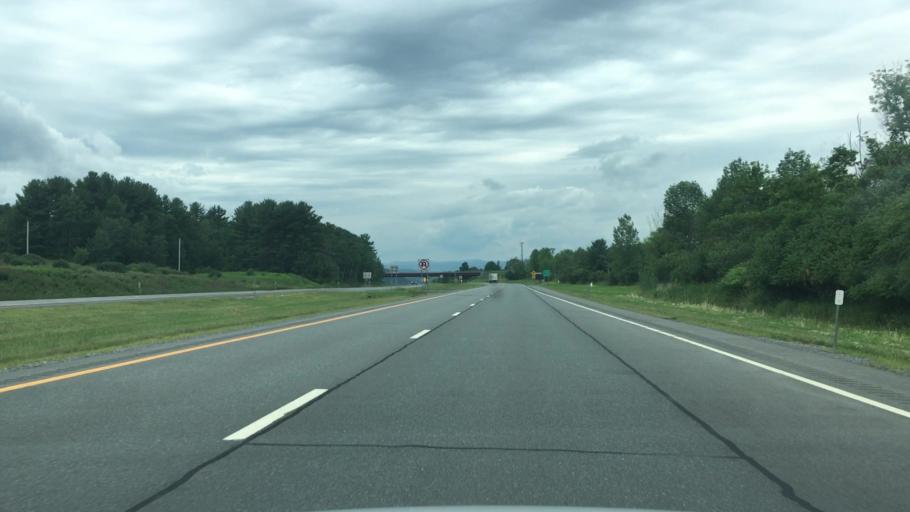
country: US
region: New York
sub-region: Schoharie County
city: Schoharie
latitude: 42.7153
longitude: -74.2690
